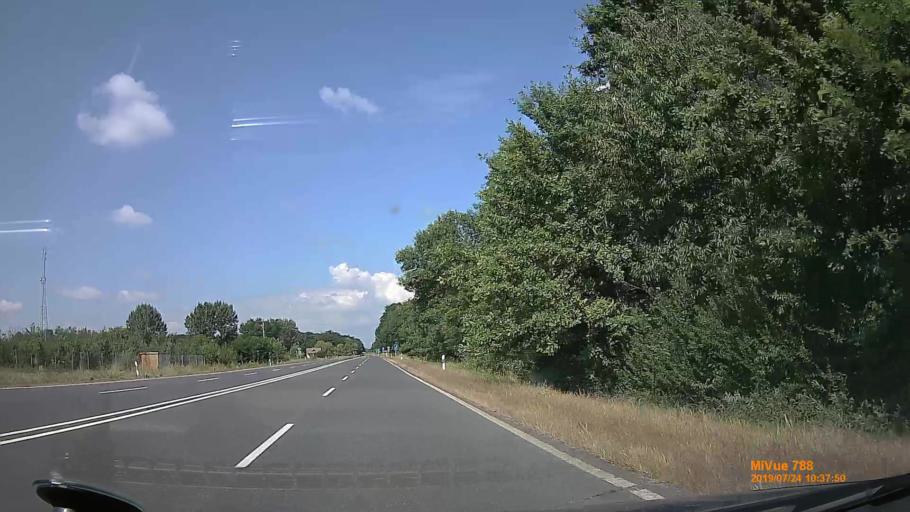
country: HU
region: Szabolcs-Szatmar-Bereg
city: Tarpa
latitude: 48.1585
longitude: 22.5512
